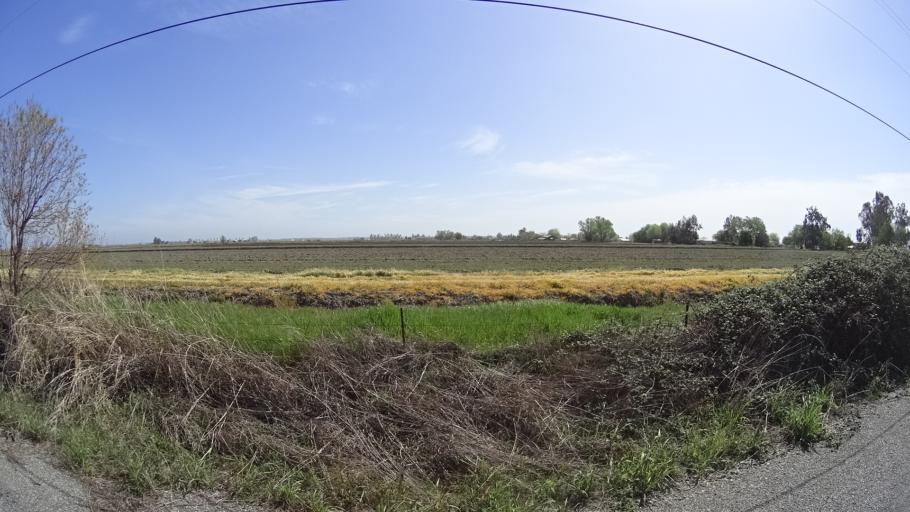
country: US
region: California
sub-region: Glenn County
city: Willows
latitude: 39.5849
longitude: -122.0555
